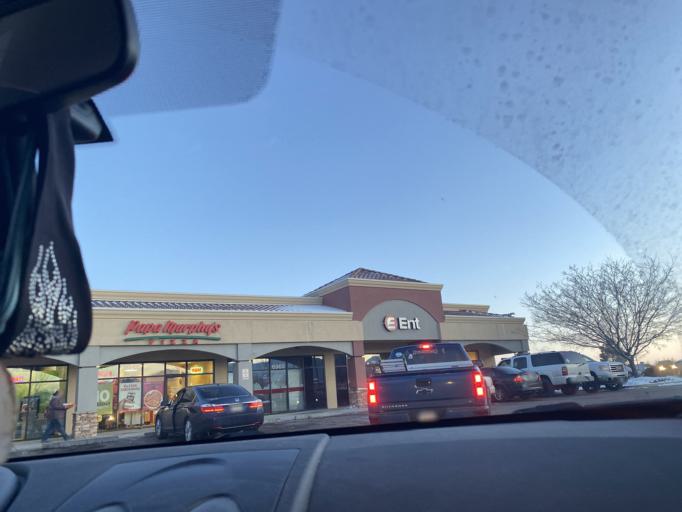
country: US
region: Colorado
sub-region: El Paso County
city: Fountain
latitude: 38.7169
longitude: -104.6971
